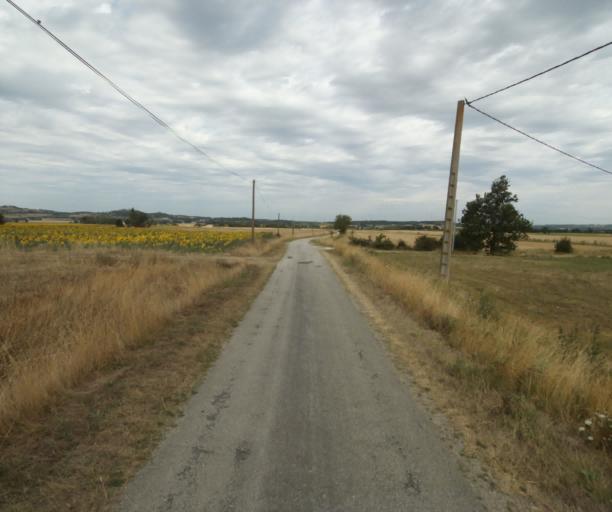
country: FR
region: Midi-Pyrenees
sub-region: Departement de la Haute-Garonne
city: Saint-Felix-Lauragais
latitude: 43.4354
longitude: 1.9375
